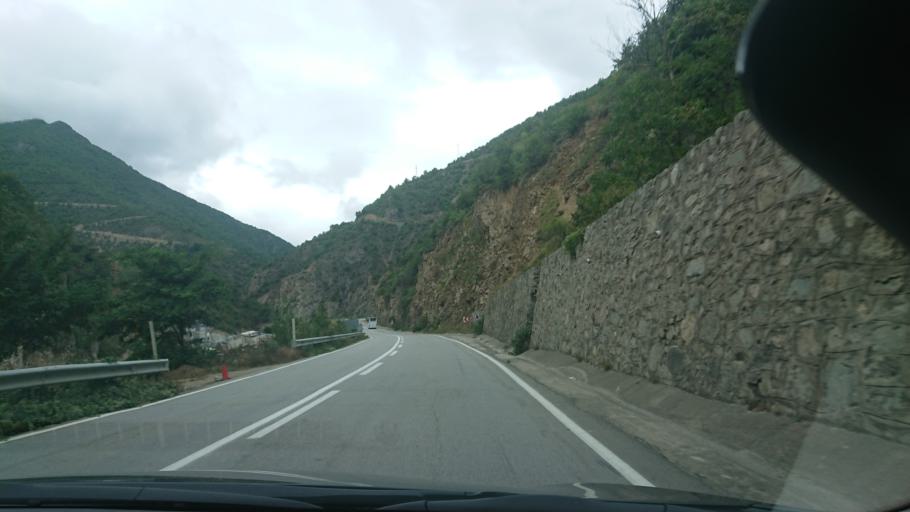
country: TR
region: Gumushane
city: Kurtun
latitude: 40.7035
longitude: 39.0748
